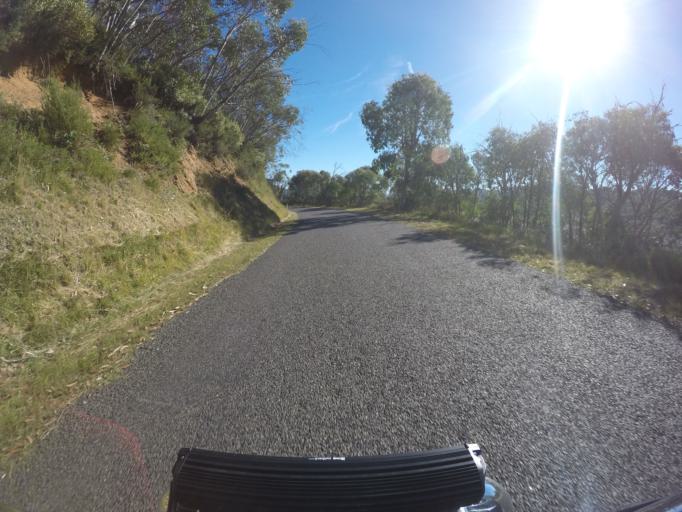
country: AU
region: New South Wales
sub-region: Snowy River
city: Jindabyne
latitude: -36.0537
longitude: 148.2726
